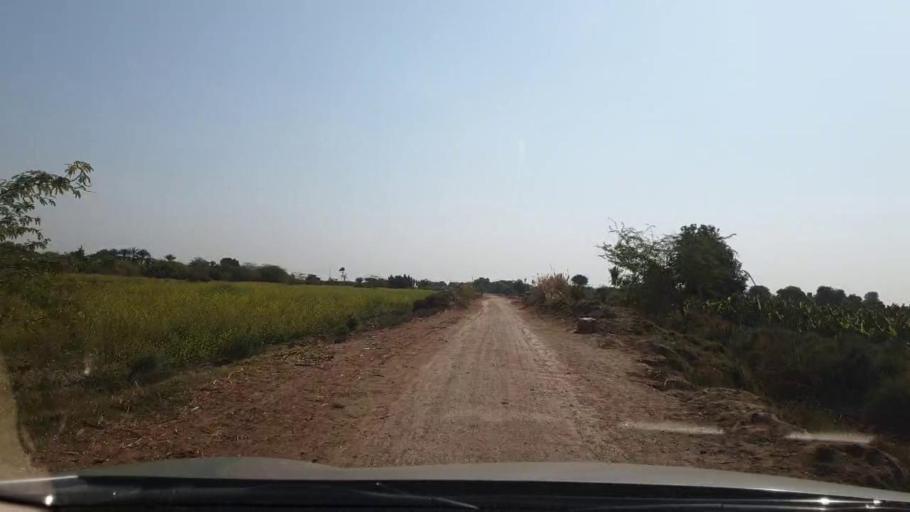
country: PK
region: Sindh
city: Mirpur Khas
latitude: 25.5932
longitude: 68.8673
